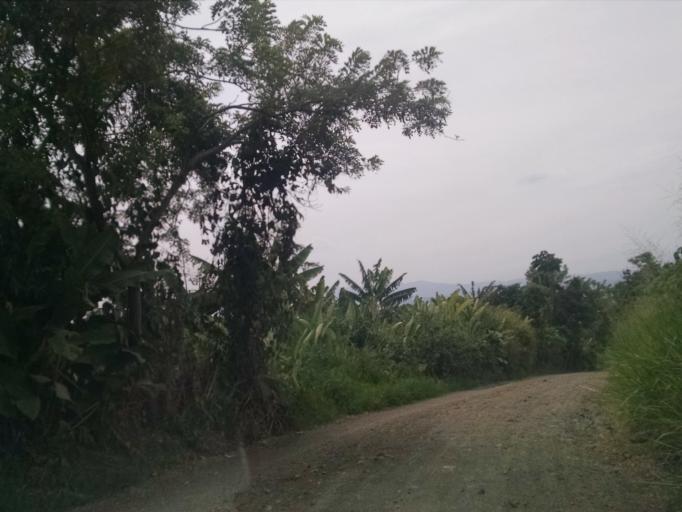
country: CO
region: Valle del Cauca
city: Ulloa
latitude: 4.7195
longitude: -75.7318
